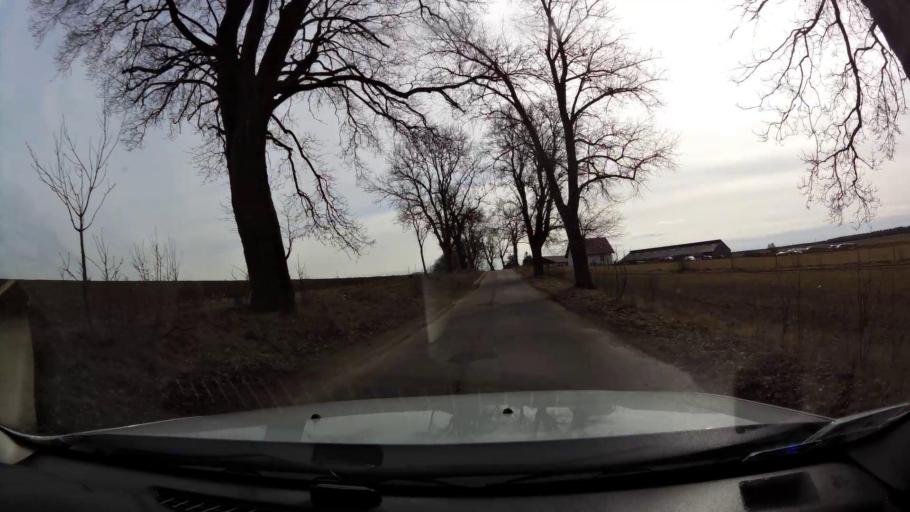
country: PL
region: West Pomeranian Voivodeship
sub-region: Powiat stargardzki
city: Insko
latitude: 53.4585
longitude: 15.6101
